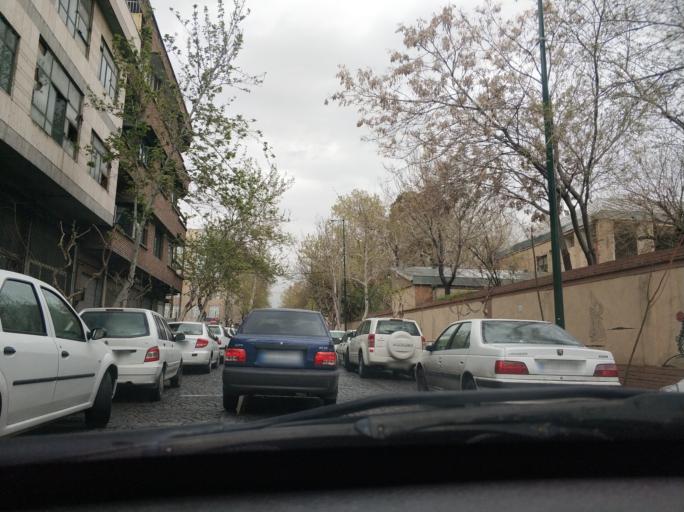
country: IR
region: Tehran
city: Tehran
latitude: 35.6910
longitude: 51.4143
